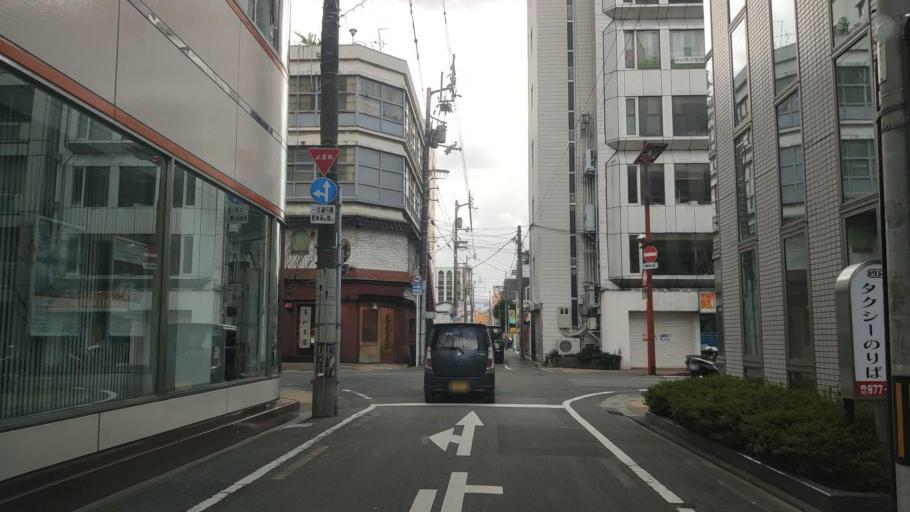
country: JP
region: Ehime
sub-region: Shikoku-chuo Shi
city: Matsuyama
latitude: 33.8385
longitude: 132.7690
